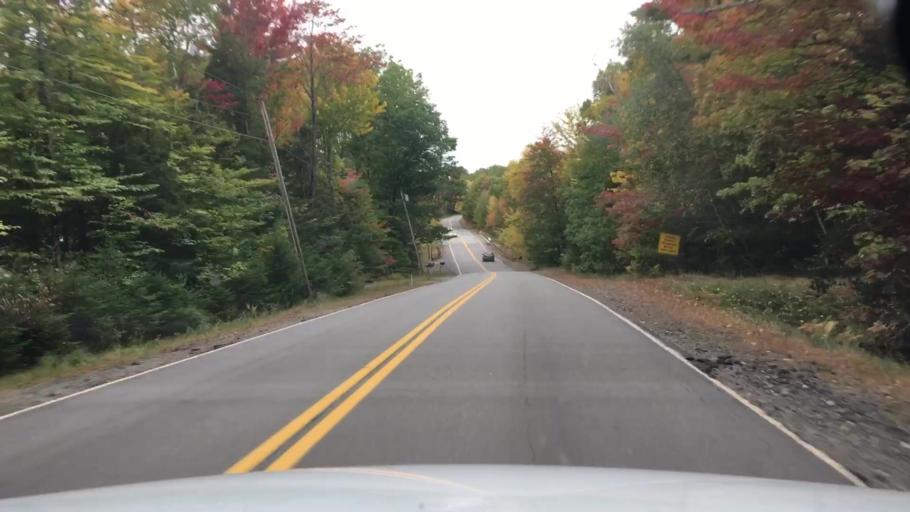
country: US
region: Maine
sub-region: Penobscot County
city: Hudson
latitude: 44.9846
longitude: -68.7907
